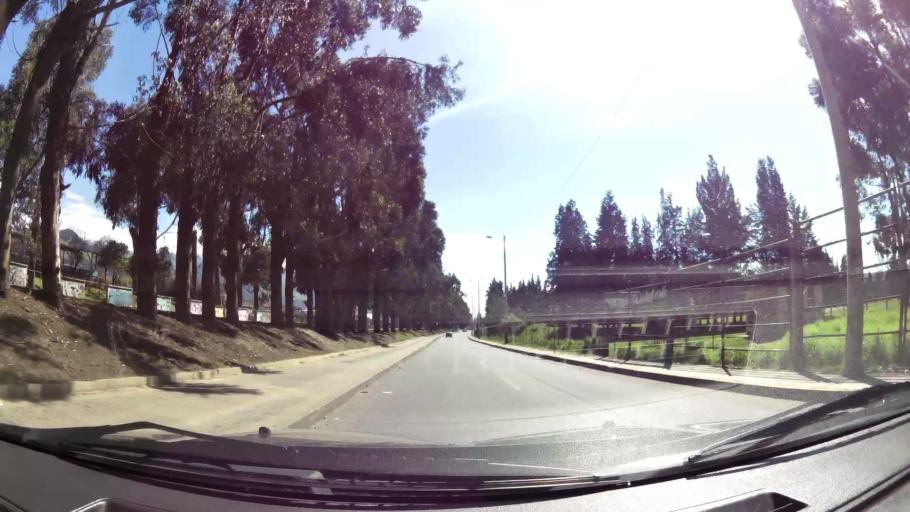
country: EC
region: Pichincha
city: Quito
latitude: -0.2869
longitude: -78.5562
